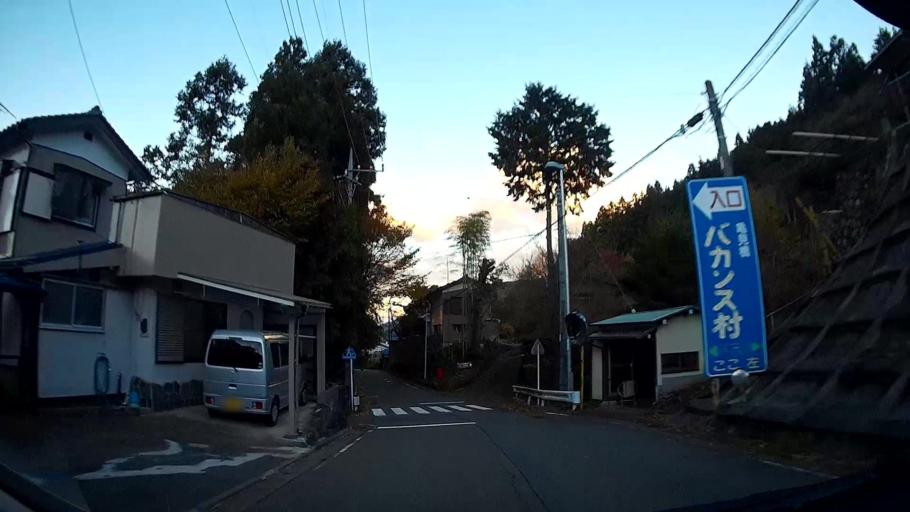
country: JP
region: Yamanashi
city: Uenohara
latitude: 35.5572
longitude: 139.1728
